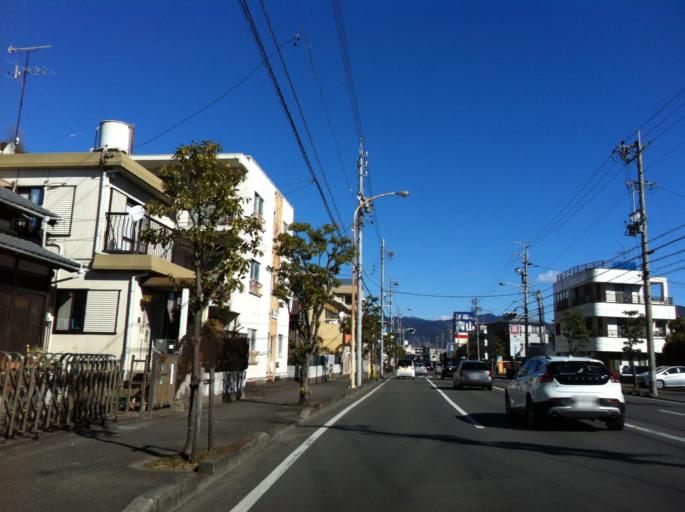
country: JP
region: Shizuoka
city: Shizuoka-shi
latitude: 34.9932
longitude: 138.3781
